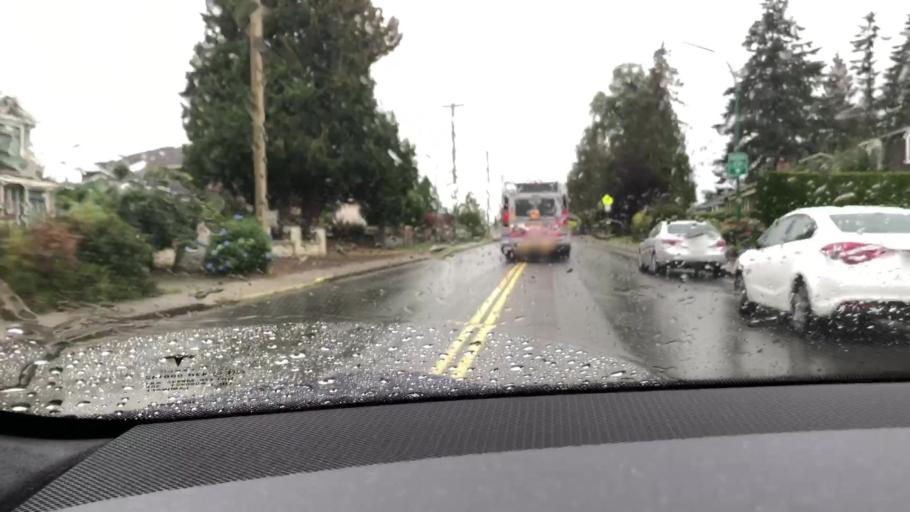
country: CA
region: British Columbia
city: New Westminster
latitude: 49.2350
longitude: -122.9056
